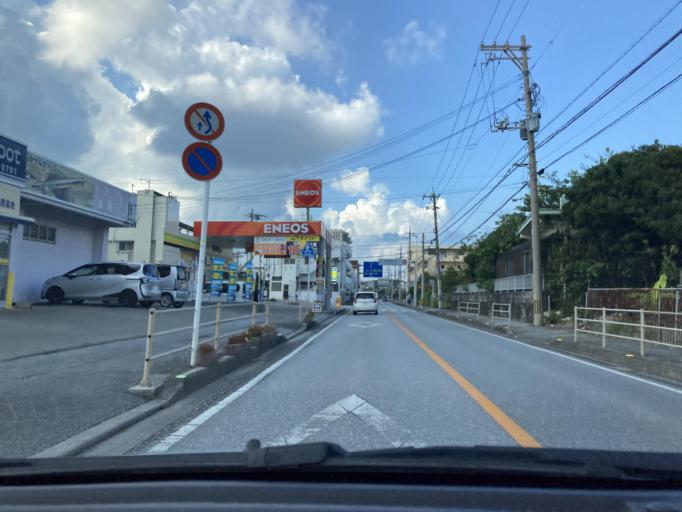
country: JP
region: Okinawa
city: Tomigusuku
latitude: 26.1845
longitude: 127.7265
